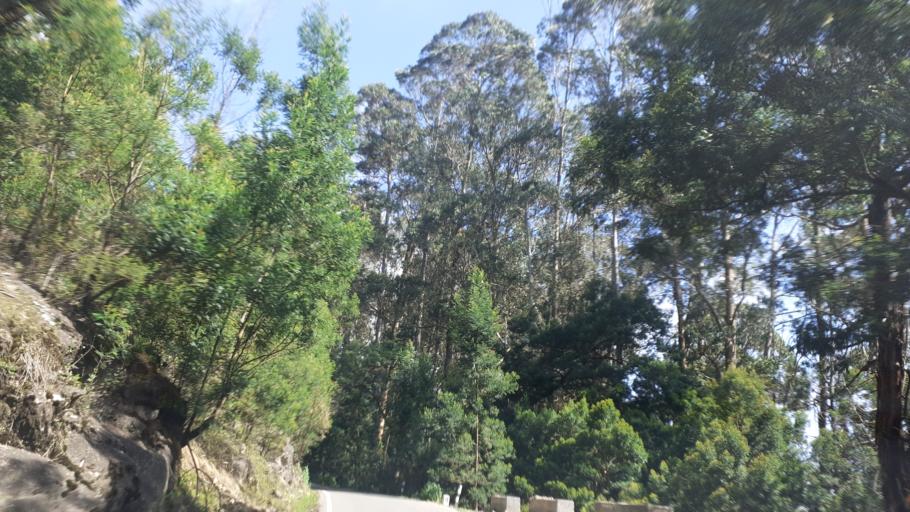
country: IN
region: Tamil Nadu
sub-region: Dindigul
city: Kodaikanal
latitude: 10.2269
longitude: 77.4233
